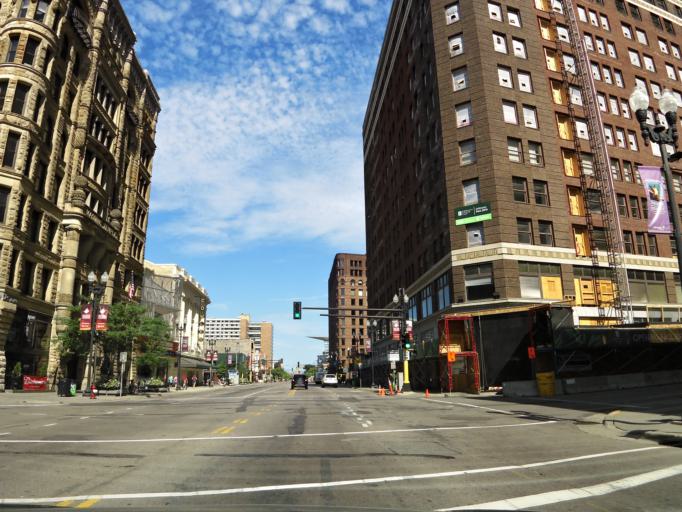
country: US
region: Minnesota
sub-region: Hennepin County
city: Minneapolis
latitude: 44.9787
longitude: -93.2738
